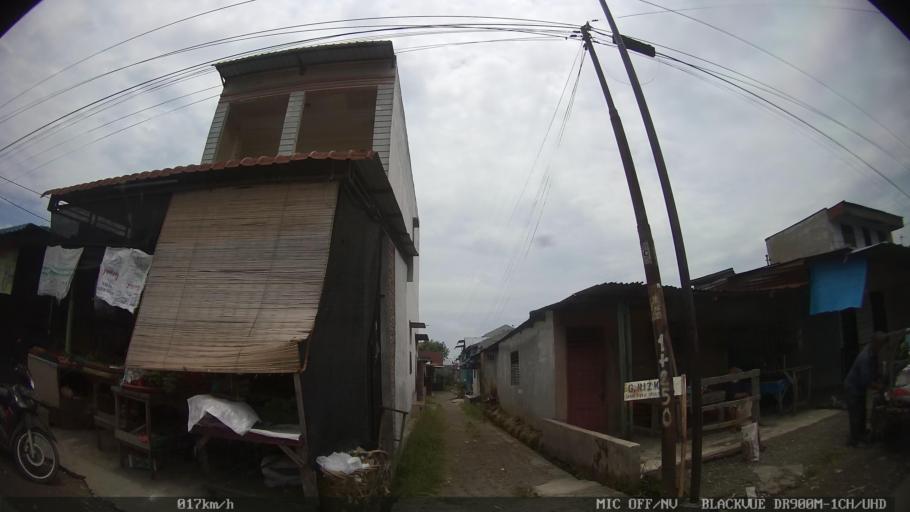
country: ID
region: North Sumatra
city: Sunggal
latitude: 3.6110
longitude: 98.5802
